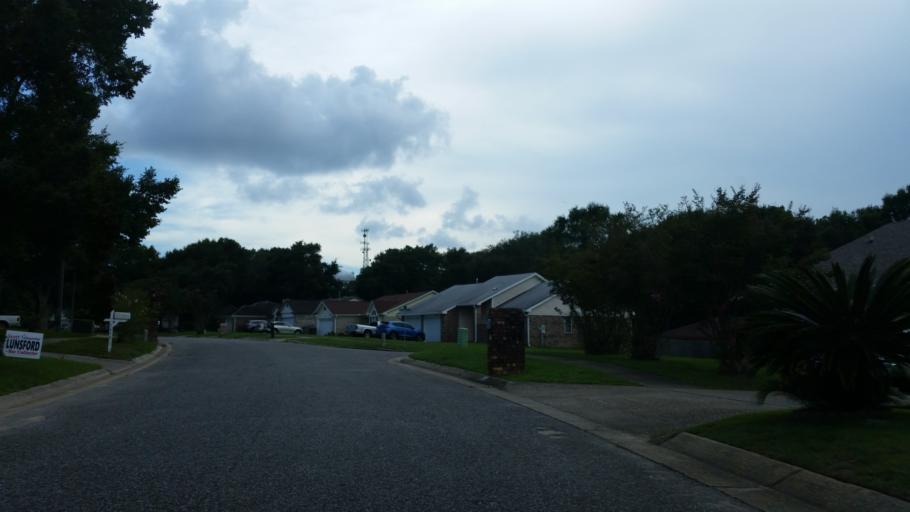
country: US
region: Florida
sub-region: Escambia County
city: Ferry Pass
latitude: 30.5058
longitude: -87.1701
